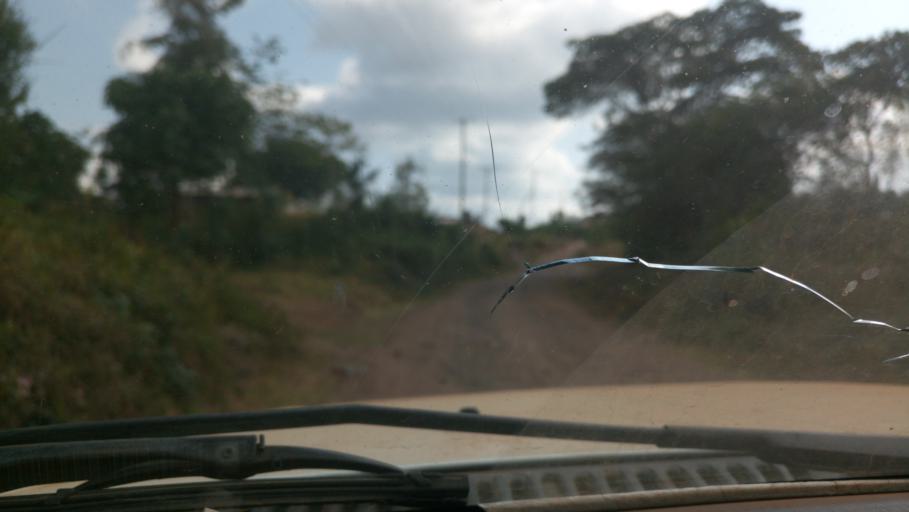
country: KE
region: Murang'a District
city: Maragua
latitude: -0.9039
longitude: 37.1189
